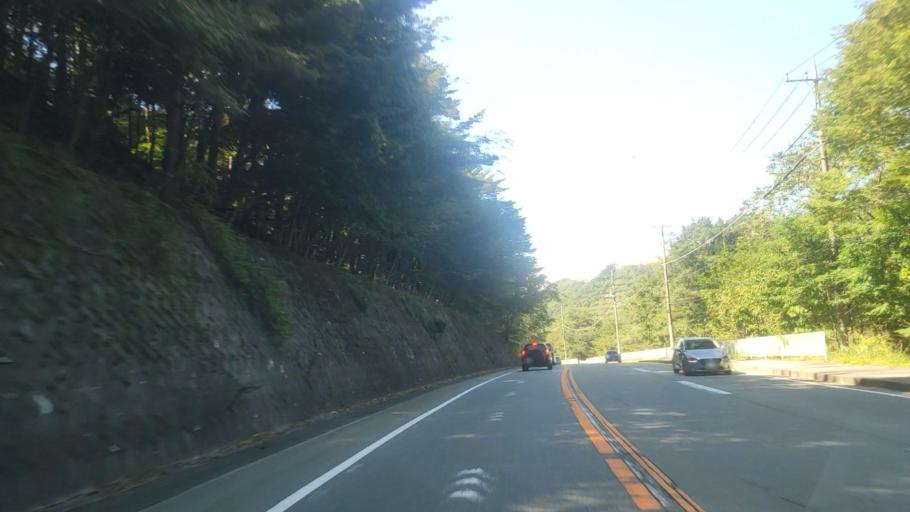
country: JP
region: Yamanashi
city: Fujikawaguchiko
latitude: 35.5877
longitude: 138.7372
